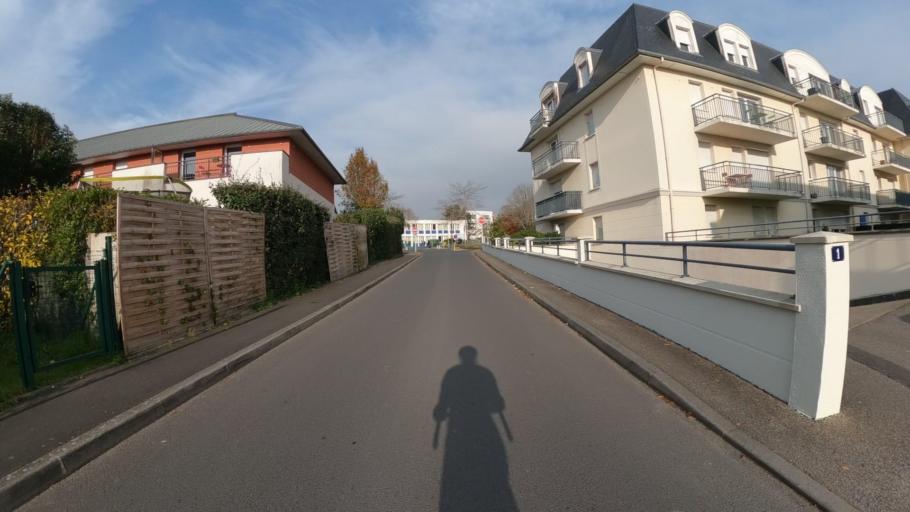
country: FR
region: Lower Normandy
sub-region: Departement du Calvados
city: Saint-Germain-la-Blanche-Herbe
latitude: 49.1886
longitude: -0.4111
